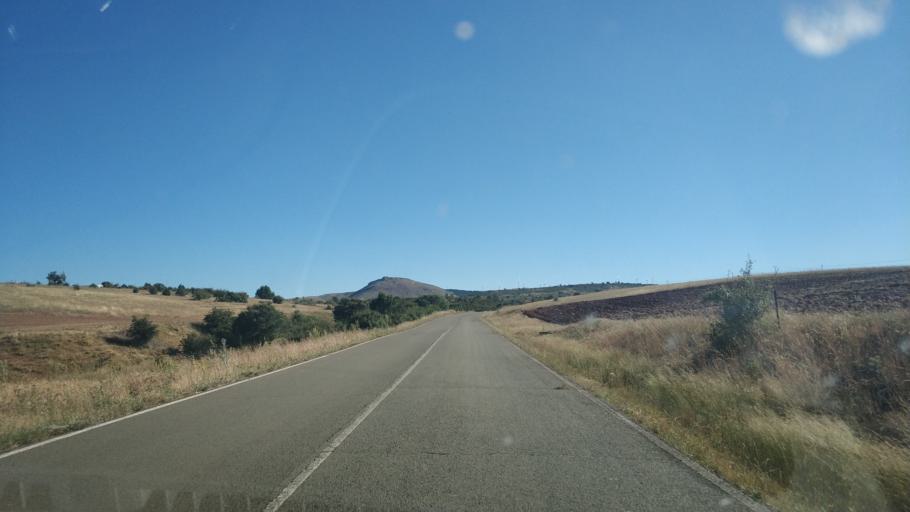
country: ES
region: Castille and Leon
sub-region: Provincia de Soria
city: Montejo de Tiermes
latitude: 41.3434
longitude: -3.1486
